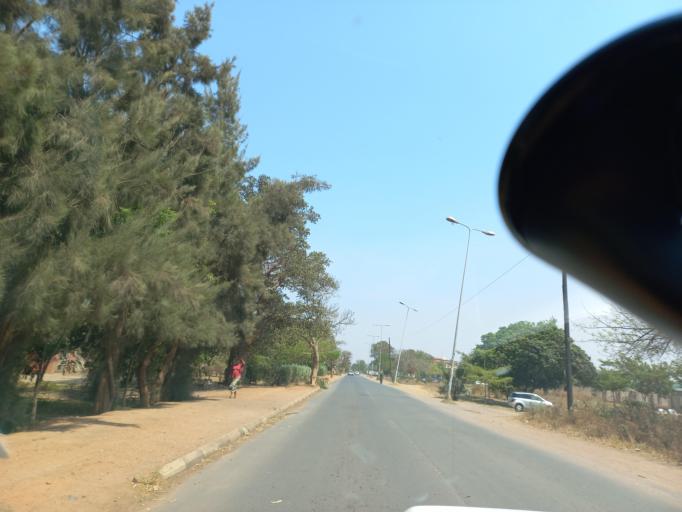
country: ZM
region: Lusaka
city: Kafue
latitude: -15.7440
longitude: 28.1679
